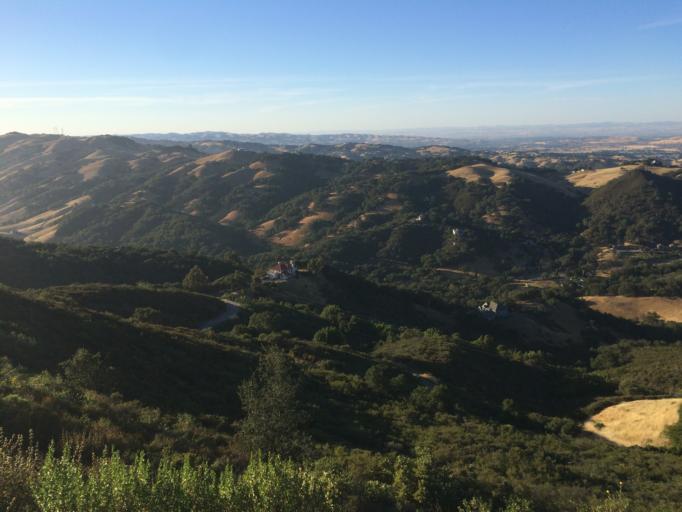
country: US
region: California
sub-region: San Luis Obispo County
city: Atascadero
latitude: 35.4515
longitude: -120.7258
